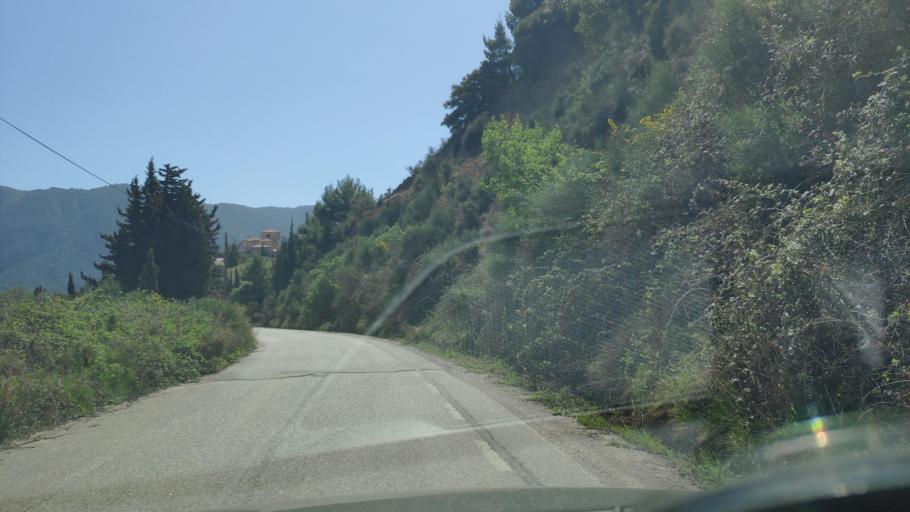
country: GR
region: West Greece
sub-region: Nomos Achaias
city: Akrata
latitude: 38.0947
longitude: 22.3219
